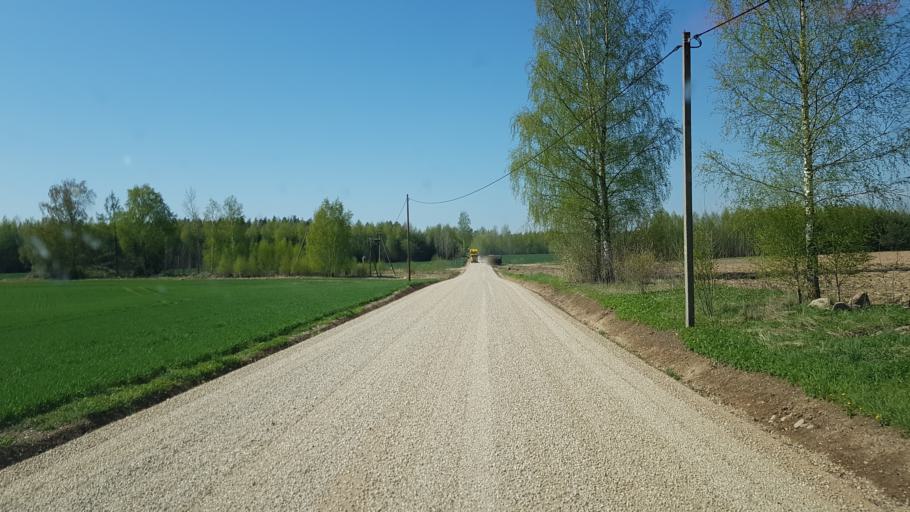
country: EE
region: Polvamaa
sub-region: Polva linn
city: Polva
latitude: 58.1245
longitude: 27.2484
